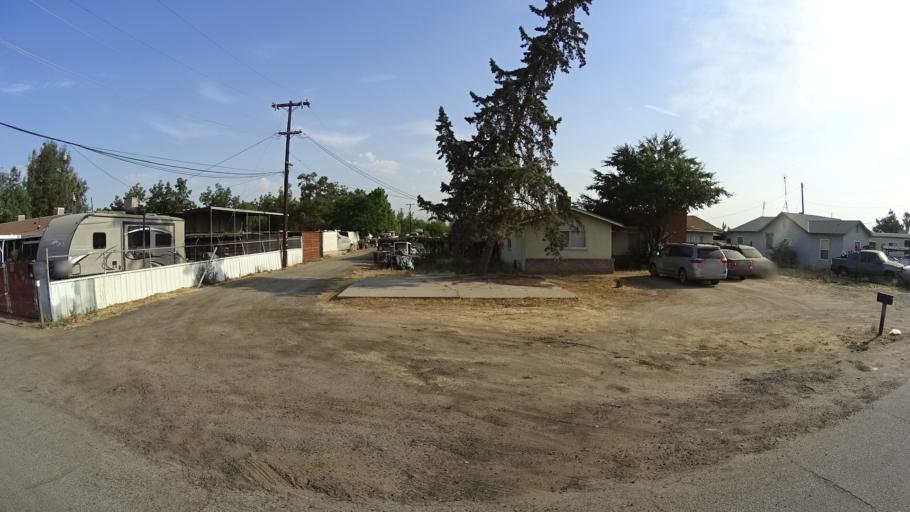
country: US
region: California
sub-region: Fresno County
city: West Park
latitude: 36.7574
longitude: -119.8503
